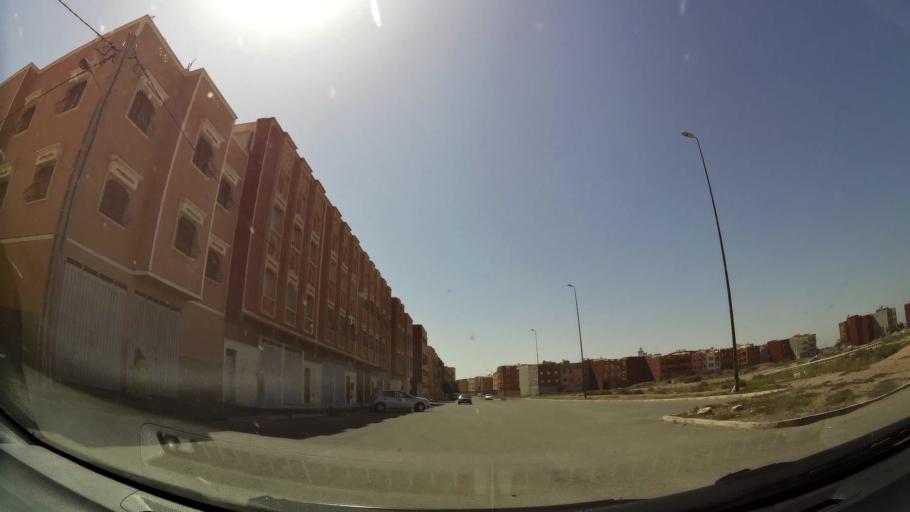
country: MA
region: Souss-Massa-Draa
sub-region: Inezgane-Ait Mellou
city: Inezgane
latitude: 30.3336
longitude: -9.5099
